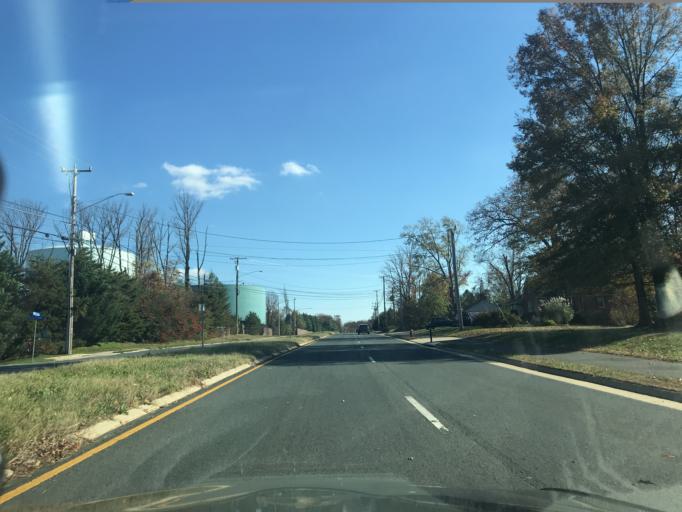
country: US
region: Virginia
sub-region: Fairfax County
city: Greenbriar
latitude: 38.8832
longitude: -77.3725
